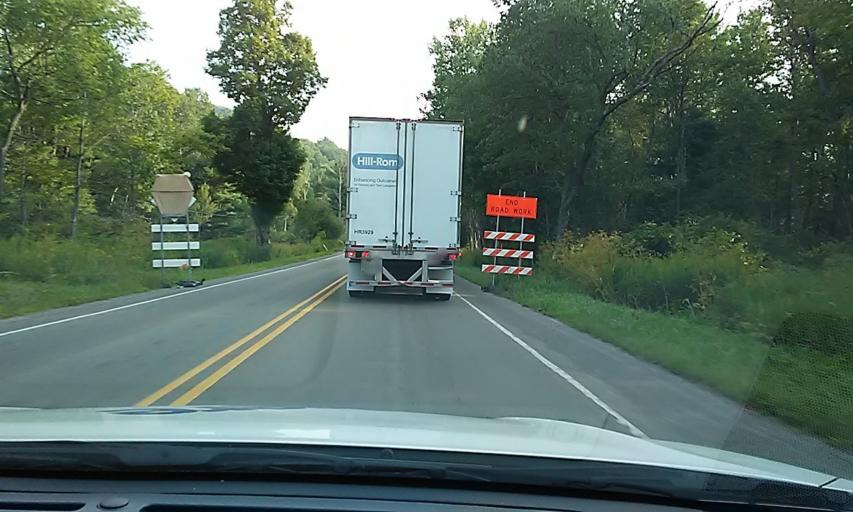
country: US
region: Pennsylvania
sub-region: McKean County
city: Smethport
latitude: 41.7482
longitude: -78.5273
